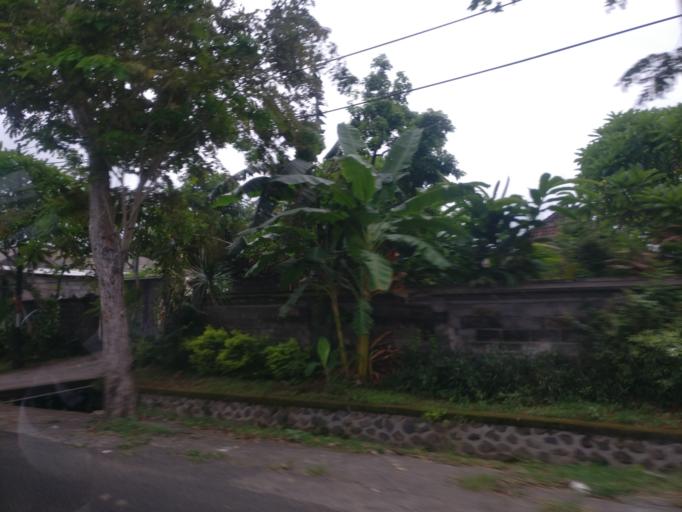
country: ID
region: Bali
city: Banjar Desa
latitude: -8.5754
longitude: 115.2963
